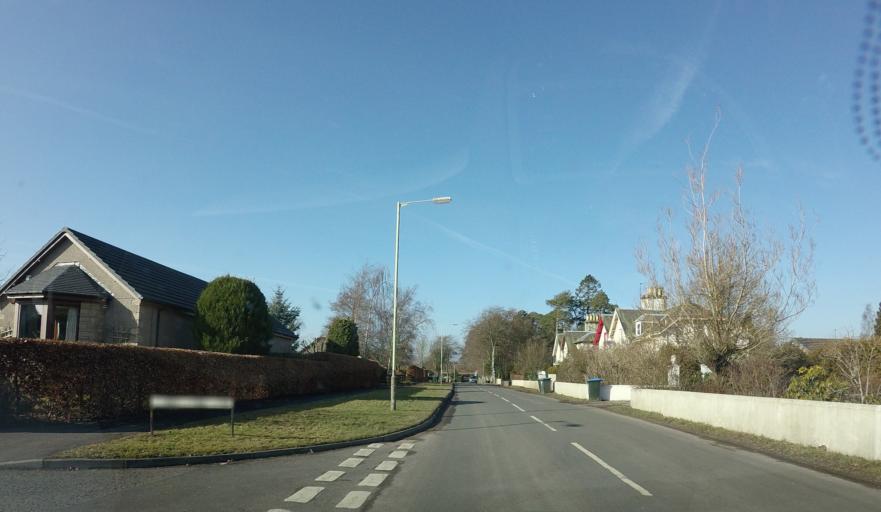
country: GB
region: Scotland
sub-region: Perth and Kinross
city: Stanley
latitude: 56.5272
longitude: -3.4581
